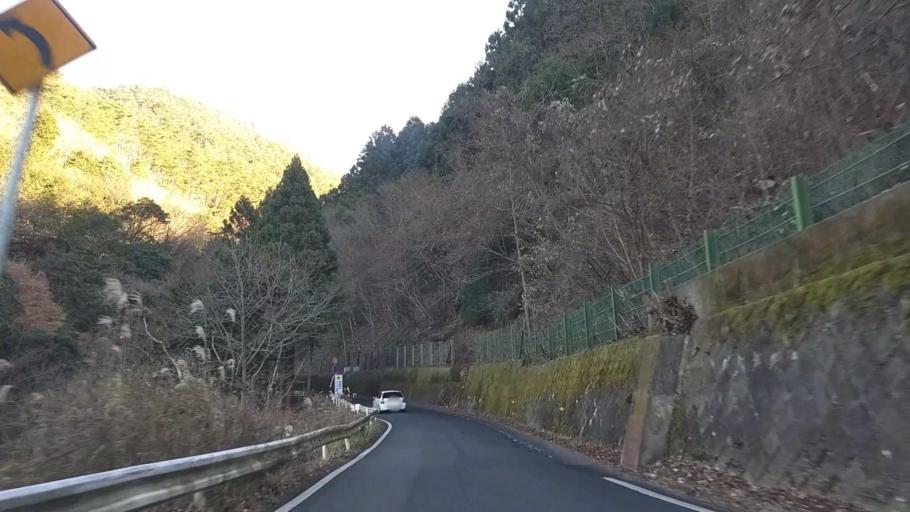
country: JP
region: Yamanashi
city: Uenohara
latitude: 35.5421
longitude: 139.1369
